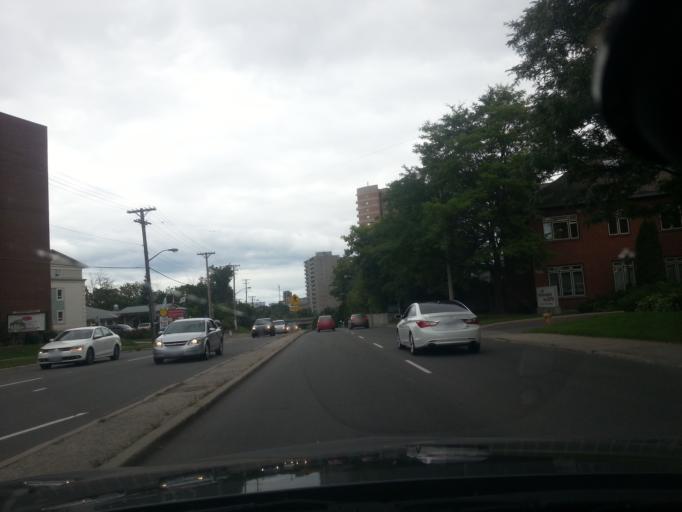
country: CA
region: Ontario
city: Ottawa
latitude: 45.3844
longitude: -75.6722
